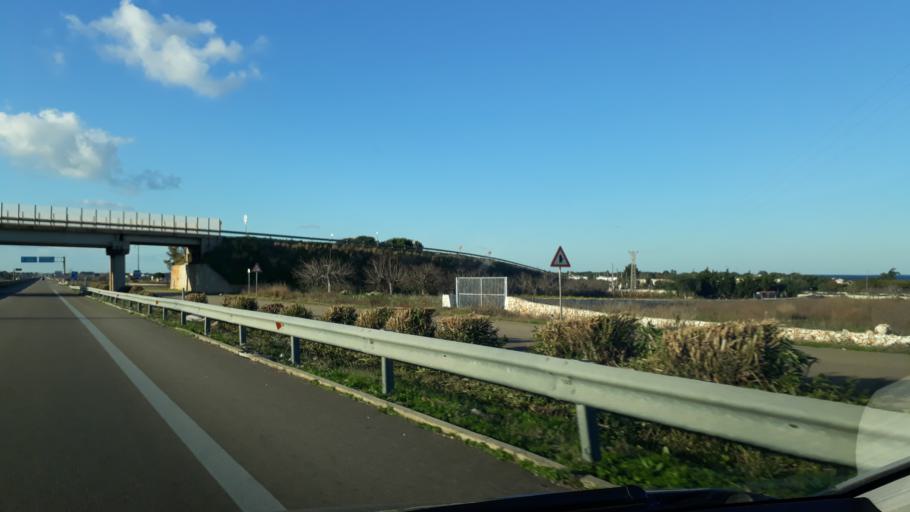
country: IT
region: Apulia
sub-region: Provincia di Brindisi
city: San Vito dei Normanni
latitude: 40.7271
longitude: 17.7401
